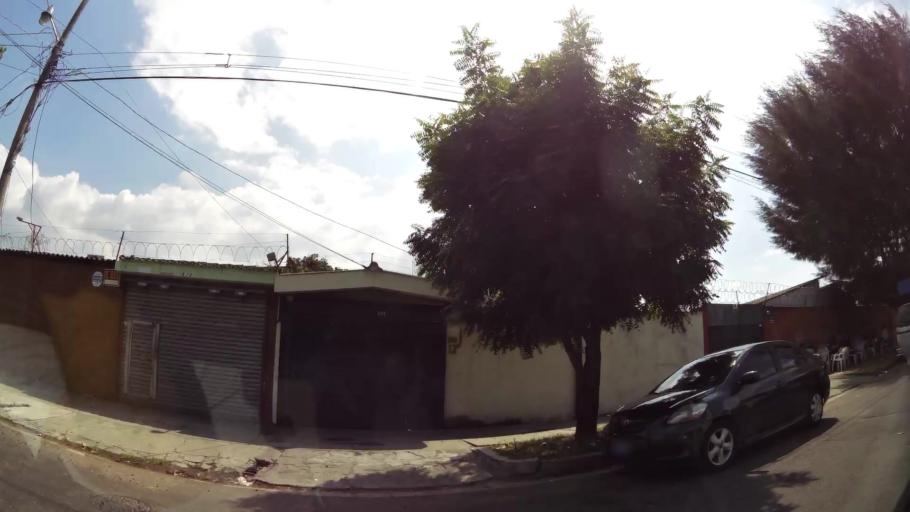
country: SV
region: San Salvador
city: Mejicanos
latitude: 13.7069
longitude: -89.2160
